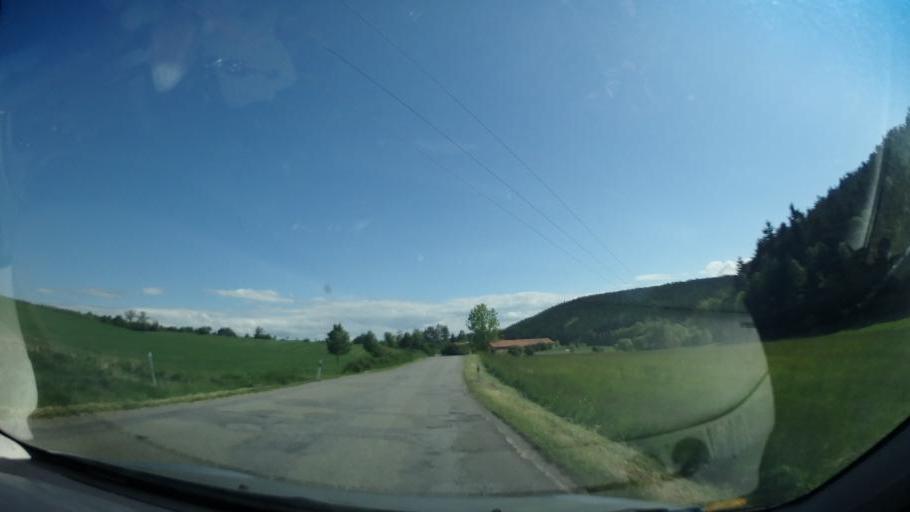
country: CZ
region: South Moravian
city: Velke Opatovice
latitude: 49.6439
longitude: 16.6152
